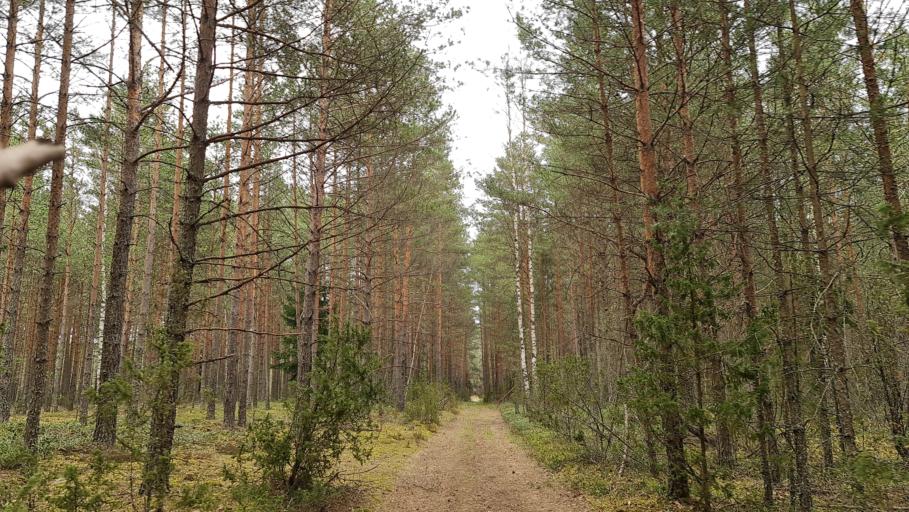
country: BY
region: Vitebsk
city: Byahoml'
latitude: 54.7446
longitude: 28.1256
